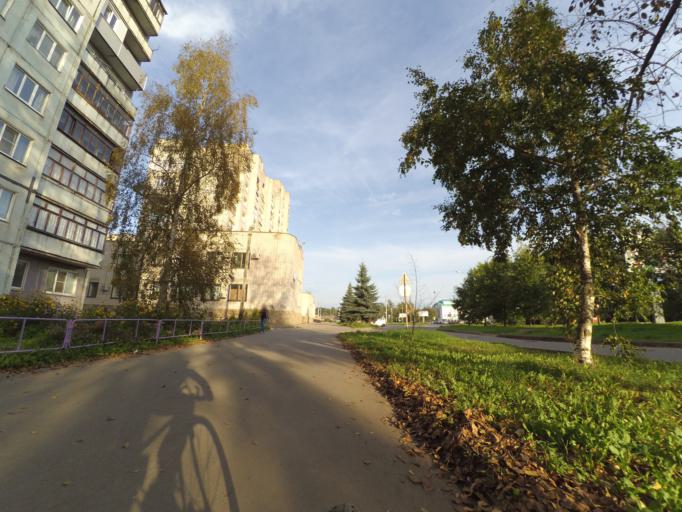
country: RU
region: Novgorod
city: Pankovka
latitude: 58.5252
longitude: 31.2272
